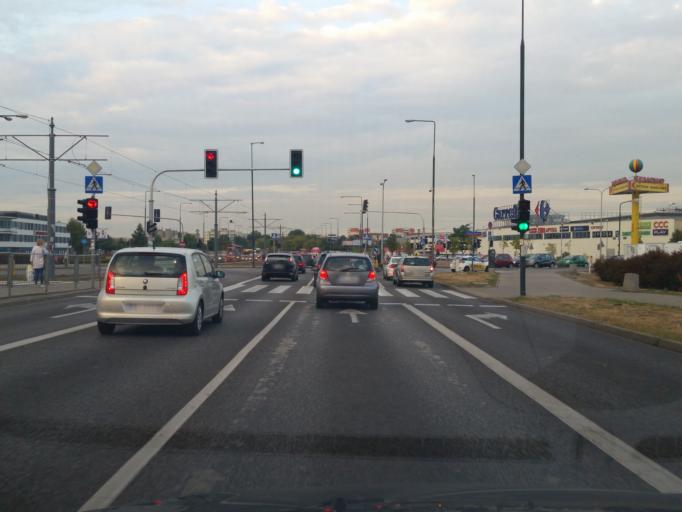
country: PL
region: Masovian Voivodeship
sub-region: Warszawa
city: Bemowo
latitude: 52.2630
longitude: 20.9272
